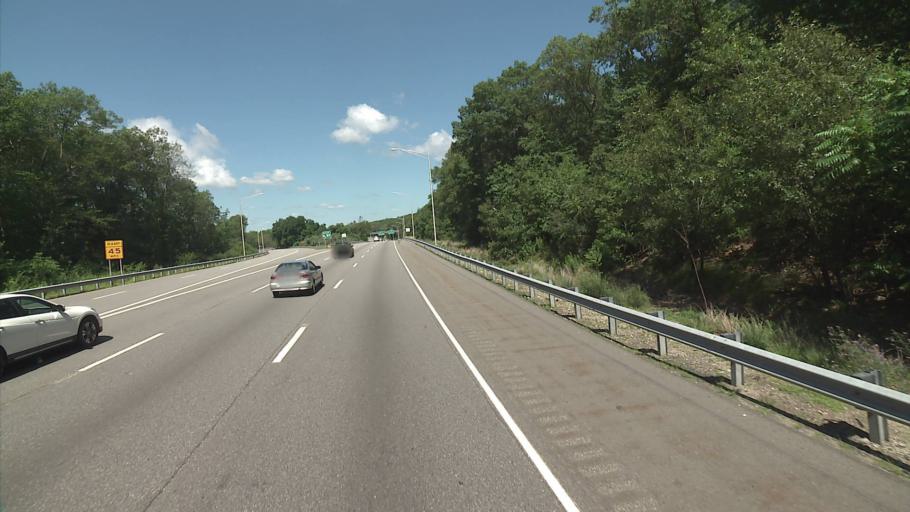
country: US
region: Connecticut
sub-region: New London County
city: Long Hill
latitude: 41.3605
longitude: -72.0528
